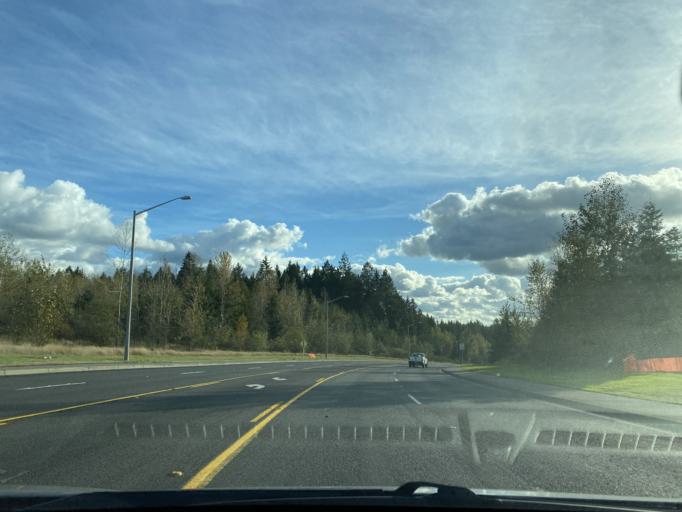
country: US
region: Washington
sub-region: Pierce County
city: South Hill
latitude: 47.0949
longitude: -122.2644
